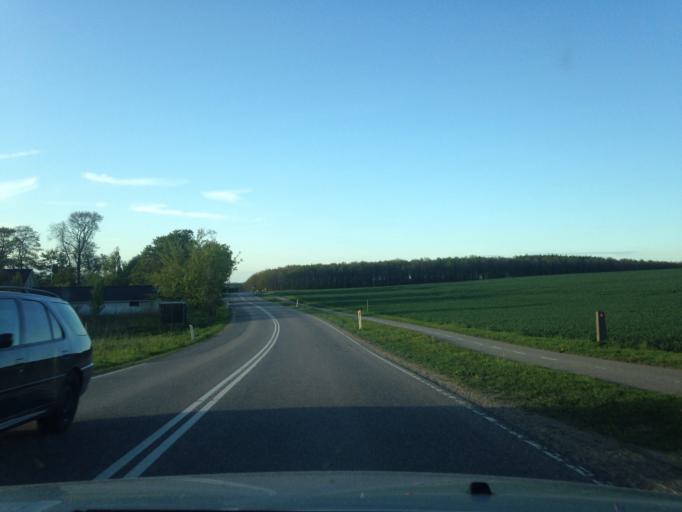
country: DK
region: Capital Region
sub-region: Hoje-Taastrup Kommune
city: Flong
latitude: 55.6337
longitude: 12.1931
